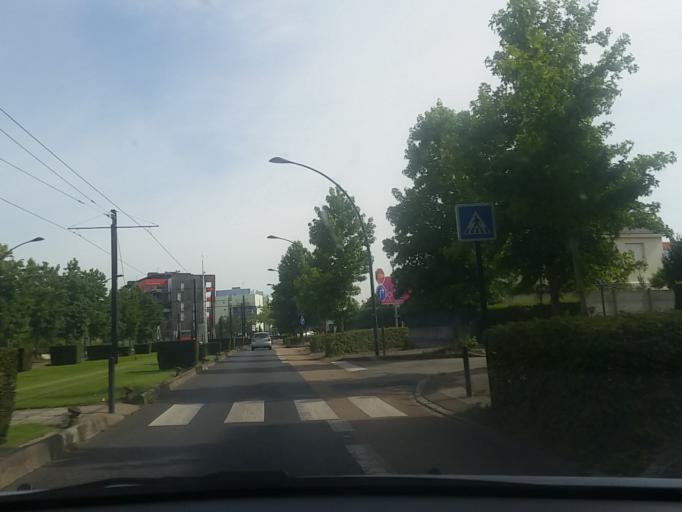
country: FR
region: Pays de la Loire
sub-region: Departement de la Loire-Atlantique
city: Bouguenais
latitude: 47.2127
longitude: -1.6083
